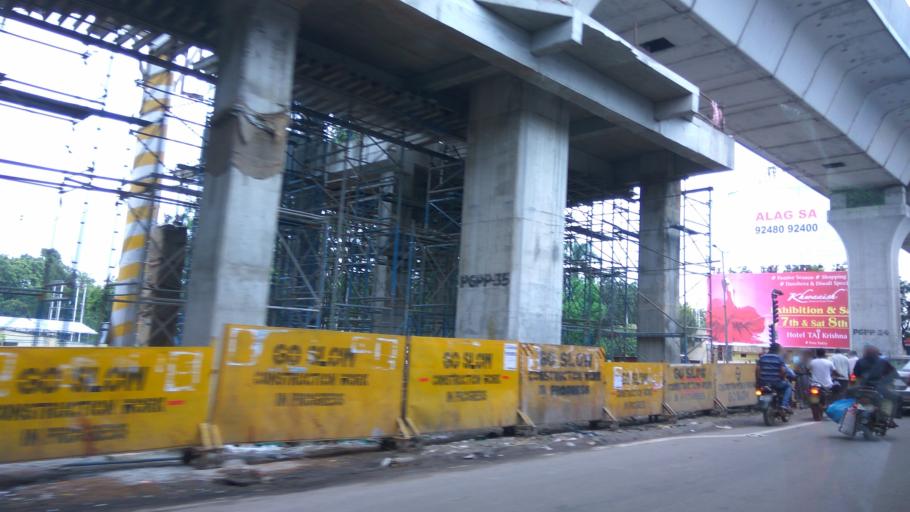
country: IN
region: Telangana
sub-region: Hyderabad
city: Malkajgiri
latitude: 17.4435
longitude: 78.4869
